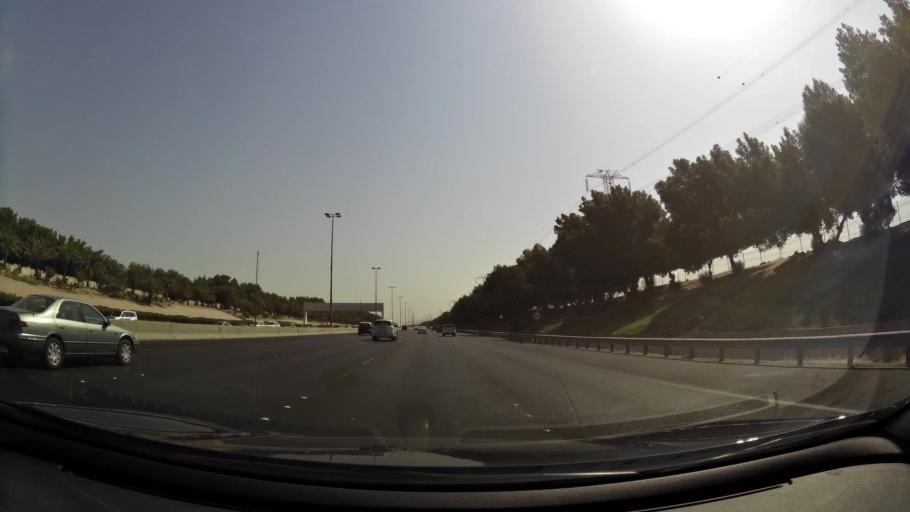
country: KW
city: Bayan
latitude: 29.2989
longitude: 48.0255
